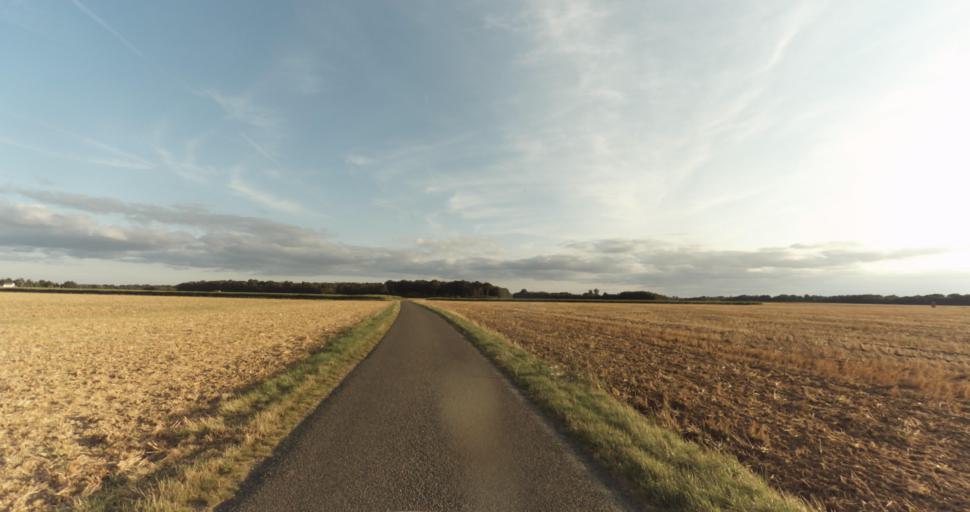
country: FR
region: Haute-Normandie
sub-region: Departement de l'Eure
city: Marcilly-sur-Eure
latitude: 48.8451
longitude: 1.2727
